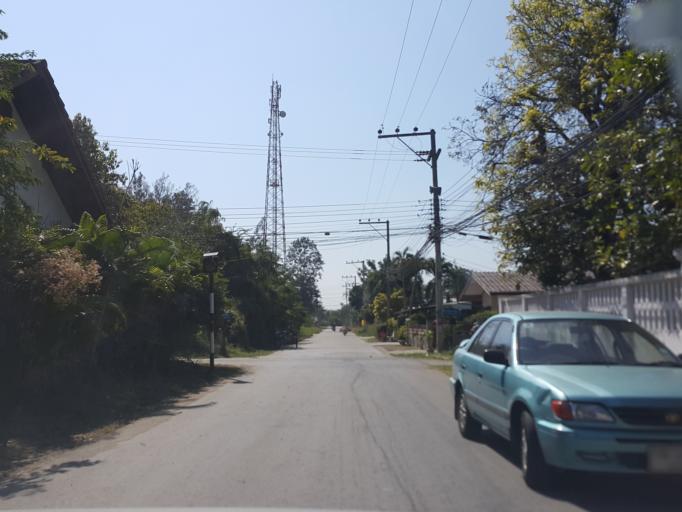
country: TH
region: Chiang Mai
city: San Kamphaeng
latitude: 18.7431
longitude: 99.1191
